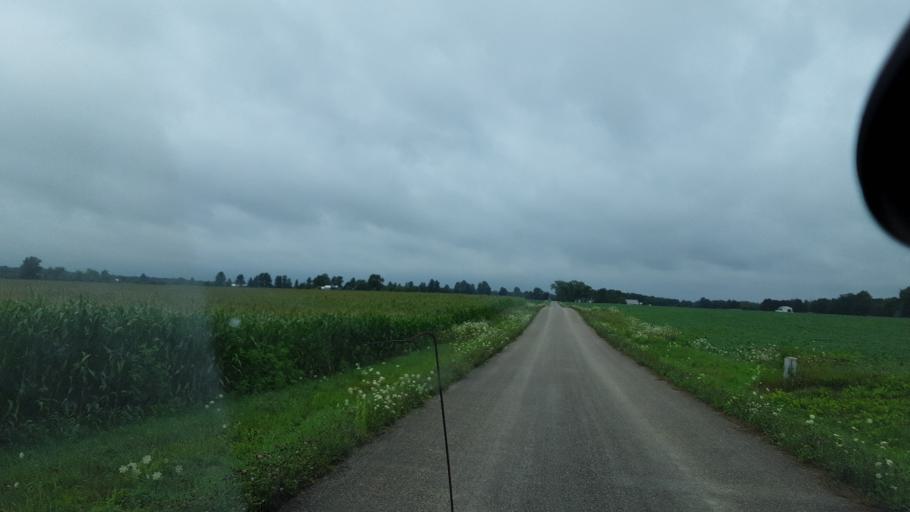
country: US
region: Indiana
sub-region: Adams County
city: Decatur
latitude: 40.8341
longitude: -84.8331
